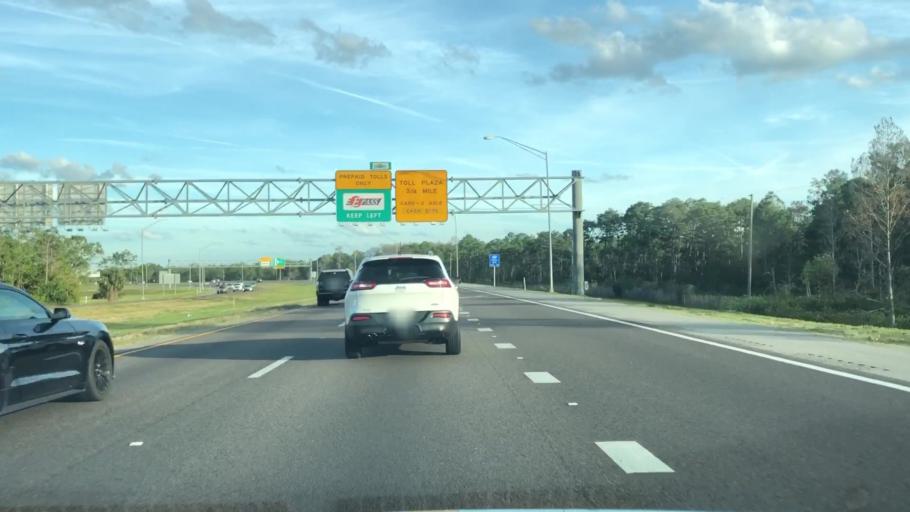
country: US
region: Florida
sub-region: Orange County
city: Hunters Creek
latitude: 28.3546
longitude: -81.4717
